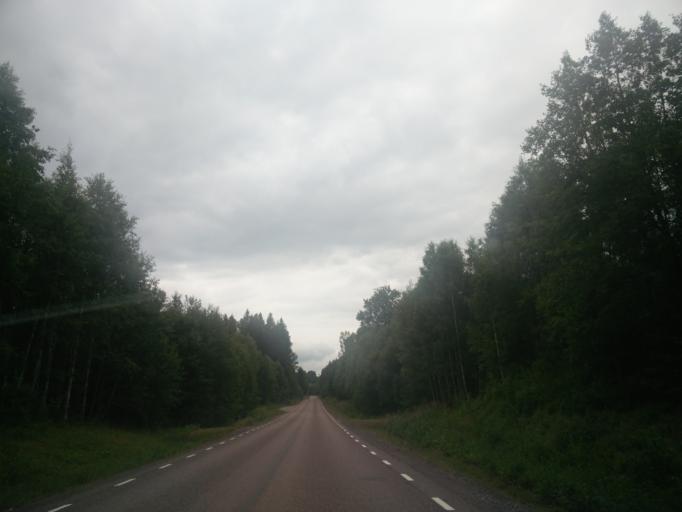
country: SE
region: Vaermland
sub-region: Torsby Kommun
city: Torsby
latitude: 59.9521
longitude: 12.7326
